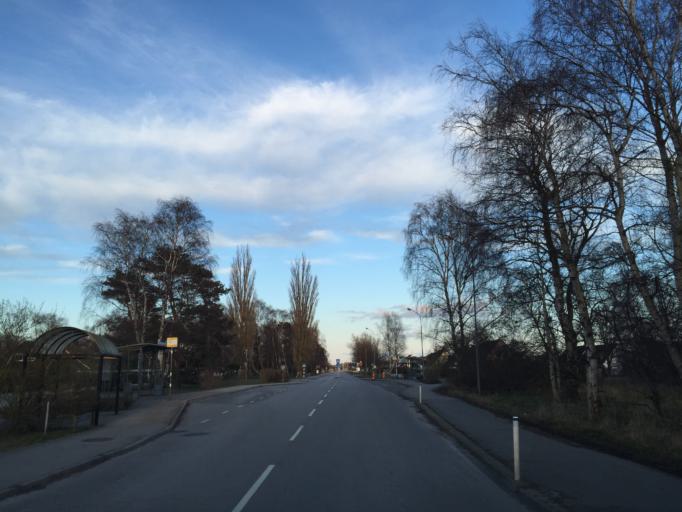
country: SE
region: Skane
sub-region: Vellinge Kommun
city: Skanor med Falsterbo
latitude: 55.4167
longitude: 12.8552
